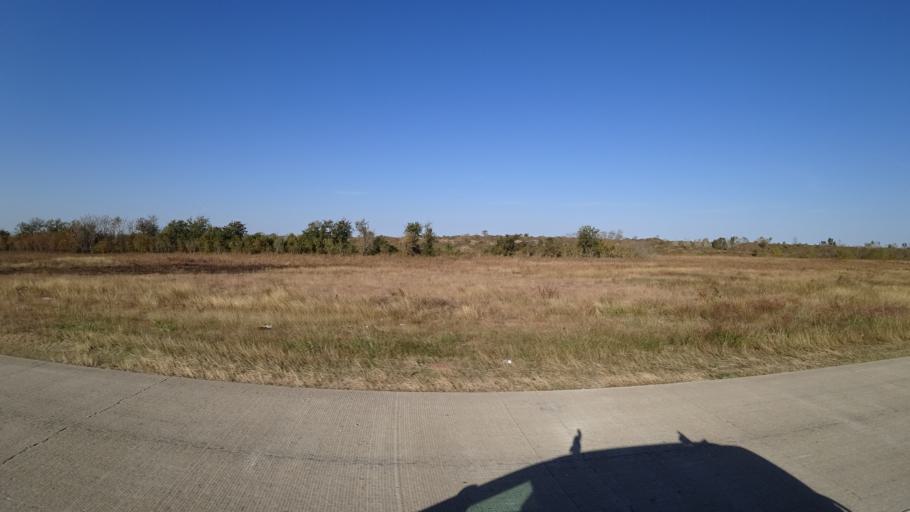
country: US
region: Texas
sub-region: Travis County
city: Hornsby Bend
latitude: 30.2404
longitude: -97.6149
